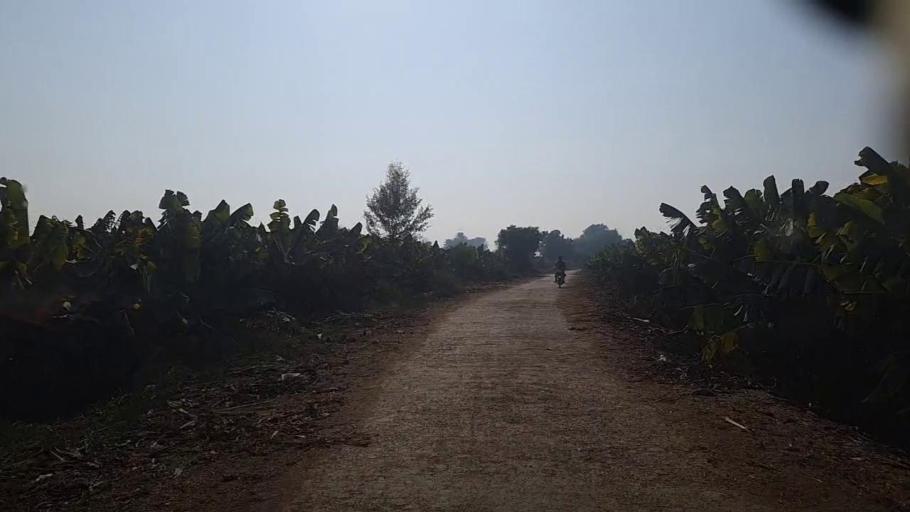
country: PK
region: Sindh
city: Kandiari
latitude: 27.0175
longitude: 68.5017
